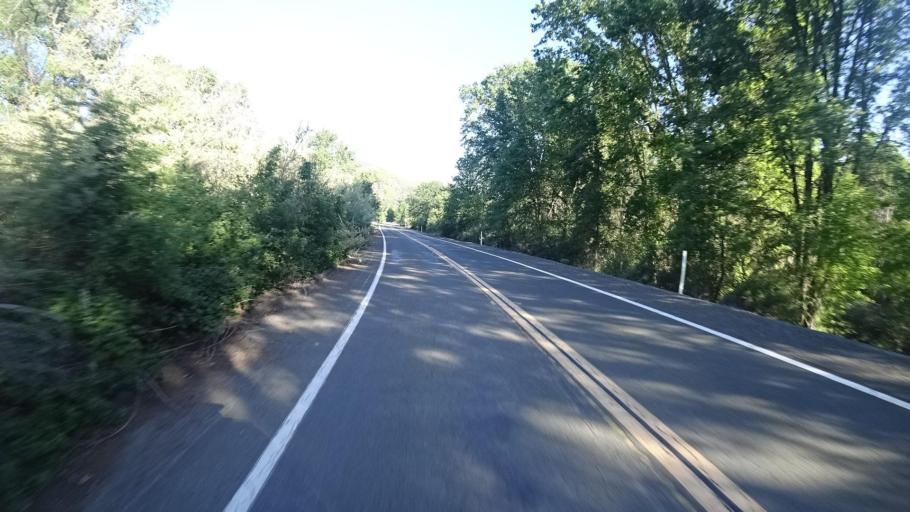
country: US
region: California
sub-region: Lake County
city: North Lakeport
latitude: 39.1058
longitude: -122.9721
